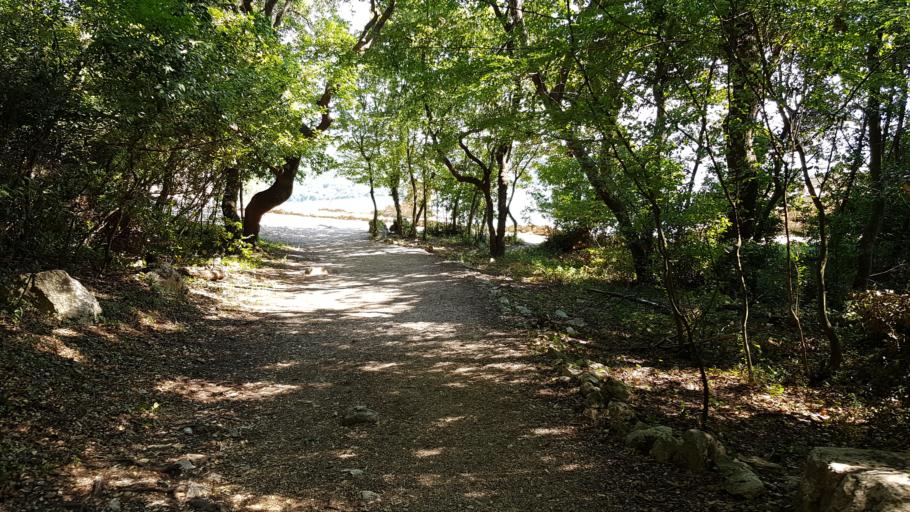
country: AL
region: Vlore
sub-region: Rrethi i Sarandes
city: Xarre
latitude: 39.7469
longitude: 20.0231
